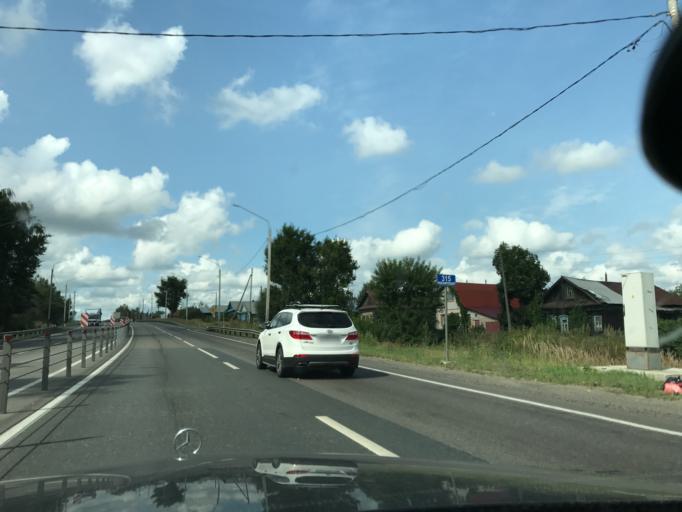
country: RU
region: Vladimir
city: Novovyazniki
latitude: 56.1802
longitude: 42.4085
